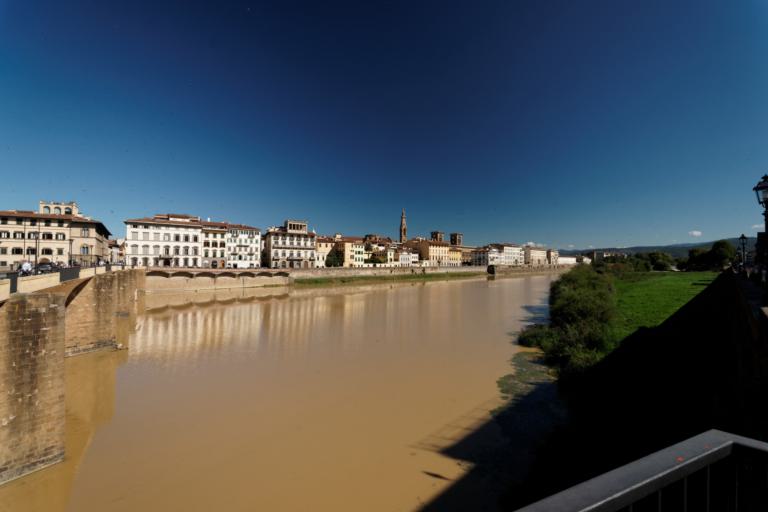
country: IT
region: Tuscany
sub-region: Province of Florence
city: Florence
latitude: 43.7655
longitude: 11.2585
